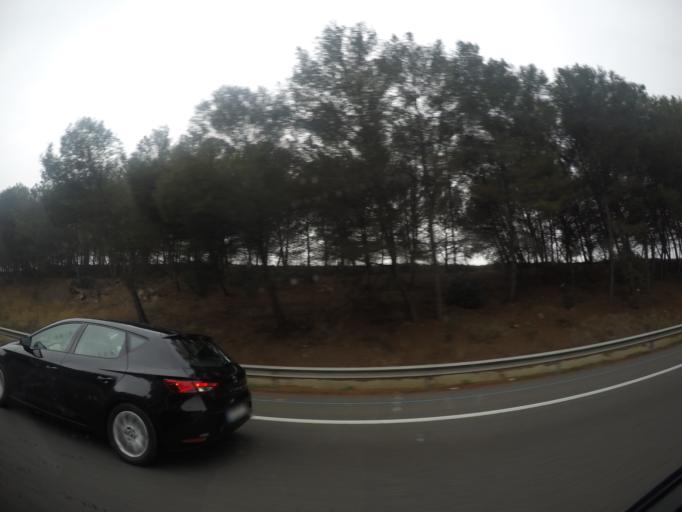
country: ES
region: Catalonia
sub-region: Provincia de Barcelona
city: Sant Sadurni d'Anoia
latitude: 41.4061
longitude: 1.7793
